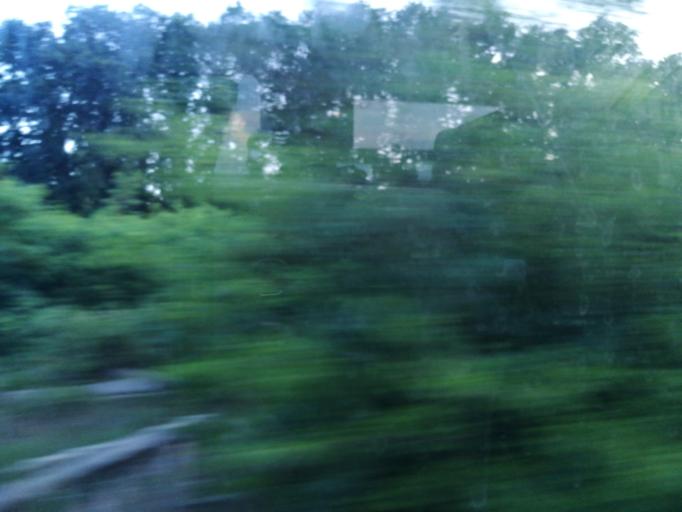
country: RO
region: Ilfov
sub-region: Comuna Buftea
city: Buciumeni
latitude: 44.5232
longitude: 25.9484
